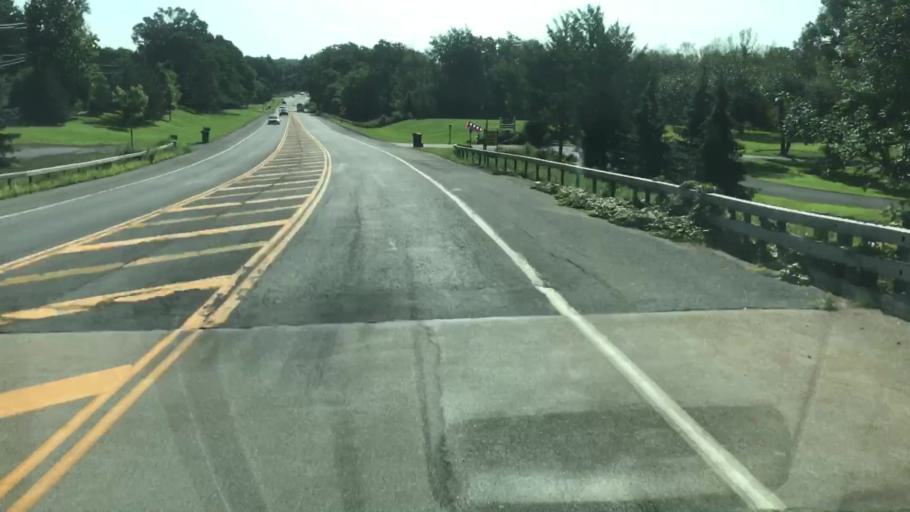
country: US
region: New York
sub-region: Onondaga County
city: Fayetteville
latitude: 43.0139
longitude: -76.0108
